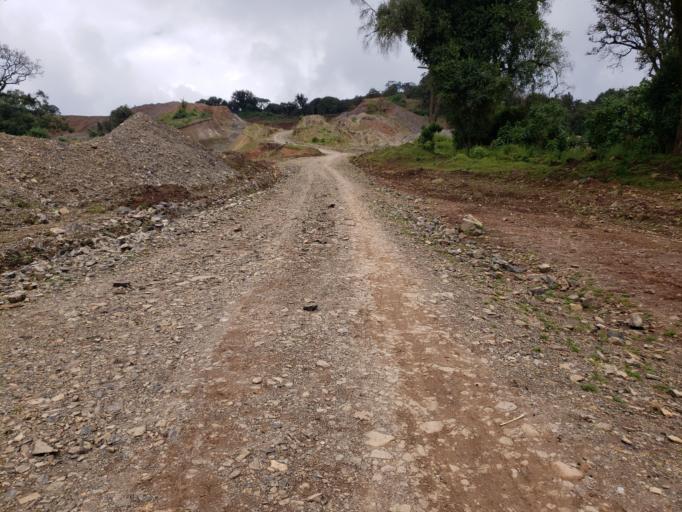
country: ET
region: Oromiya
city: Dodola
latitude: 6.6491
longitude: 39.3675
